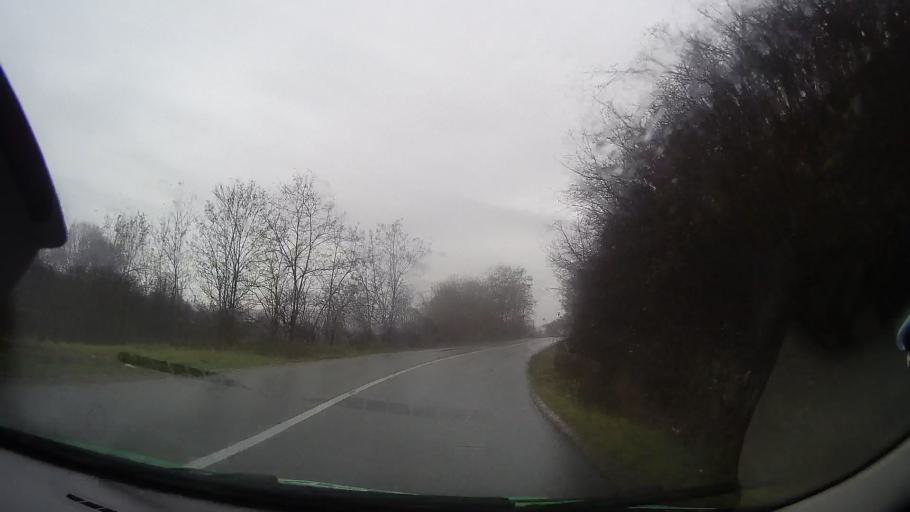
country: RO
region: Bistrita-Nasaud
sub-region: Comuna Mariselu
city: Mariselu
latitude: 47.0124
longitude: 24.5121
